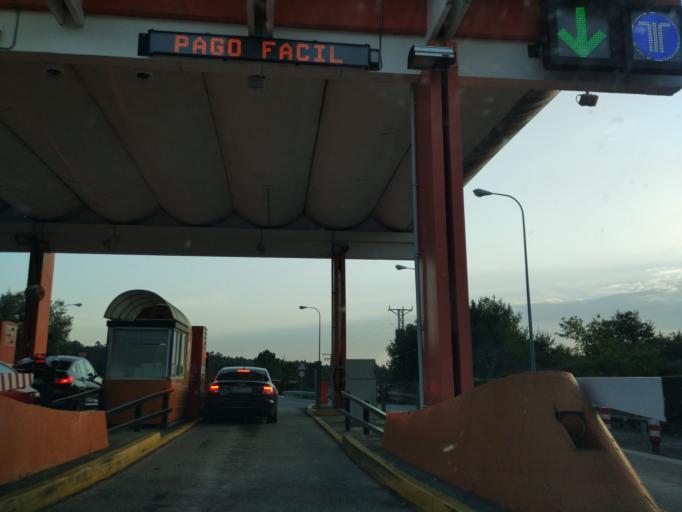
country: ES
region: Galicia
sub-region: Provincia da Coruna
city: Padron
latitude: 42.7326
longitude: -8.6404
